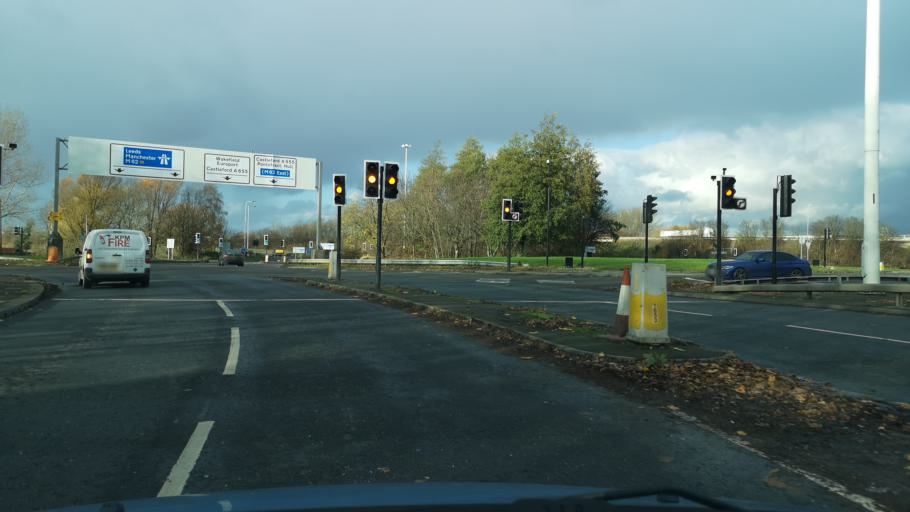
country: GB
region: England
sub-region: City and Borough of Wakefield
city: Normanton
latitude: 53.7072
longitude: -1.3971
